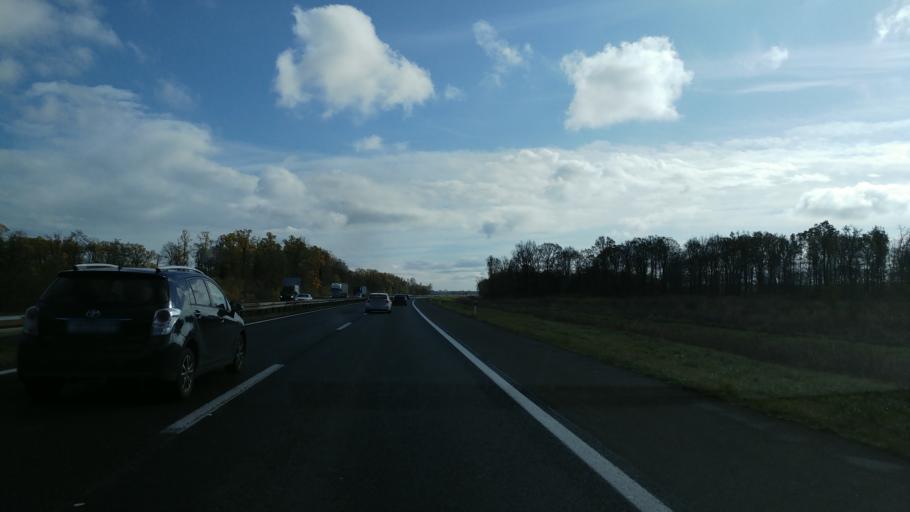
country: HR
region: Zagrebacka
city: Lupoglav
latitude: 45.7411
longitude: 16.3267
